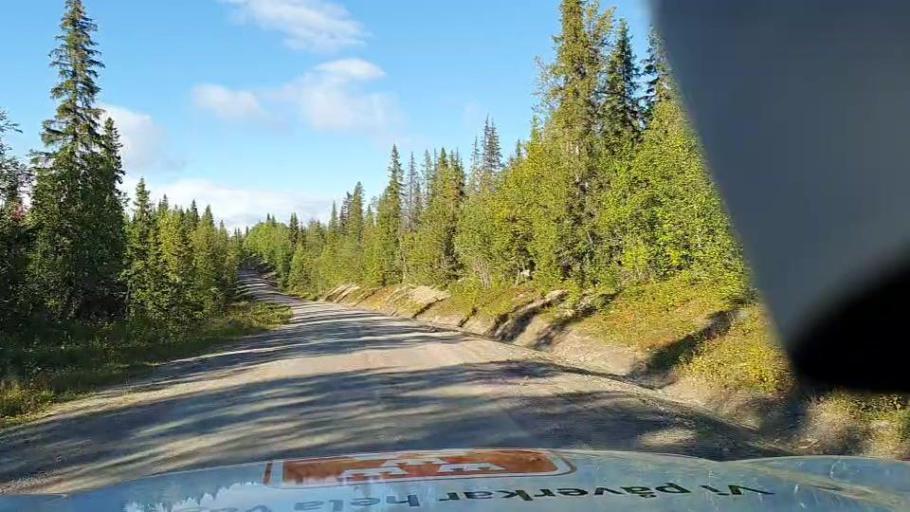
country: SE
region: Jaemtland
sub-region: Stroemsunds Kommun
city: Stroemsund
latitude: 64.5593
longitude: 15.0947
